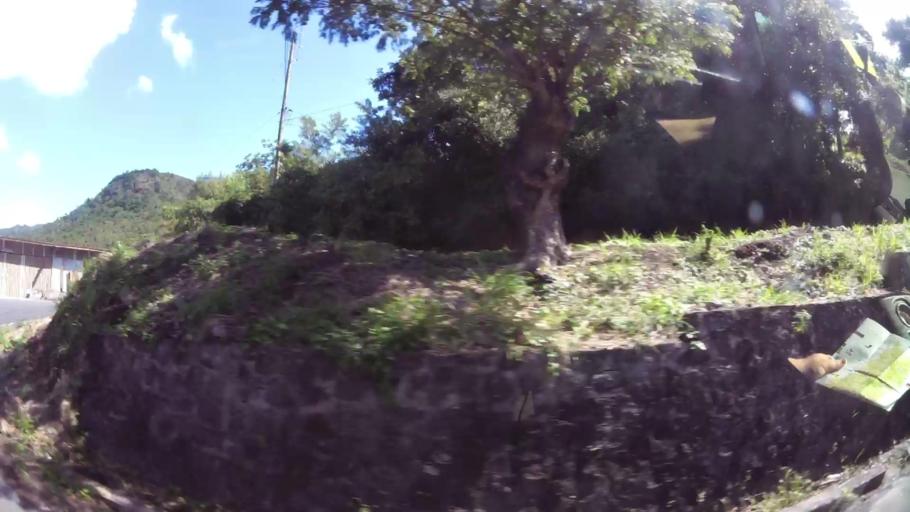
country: DM
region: Saint Paul
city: Mahaut
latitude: 15.3410
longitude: -61.3853
